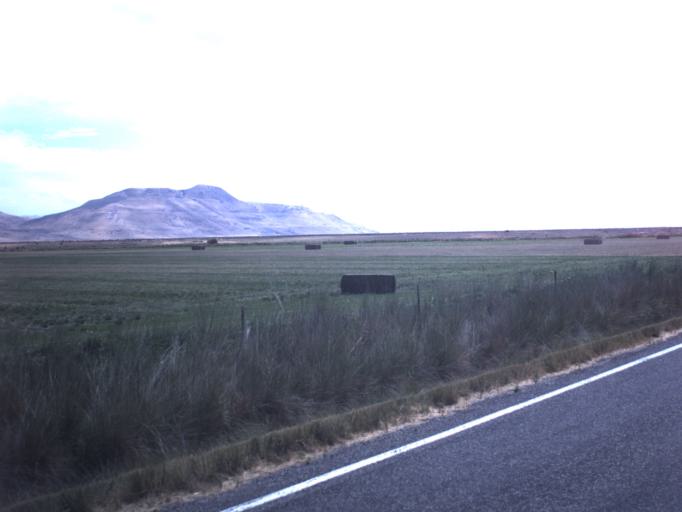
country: US
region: Utah
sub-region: Box Elder County
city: Tremonton
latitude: 41.6401
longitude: -112.3140
